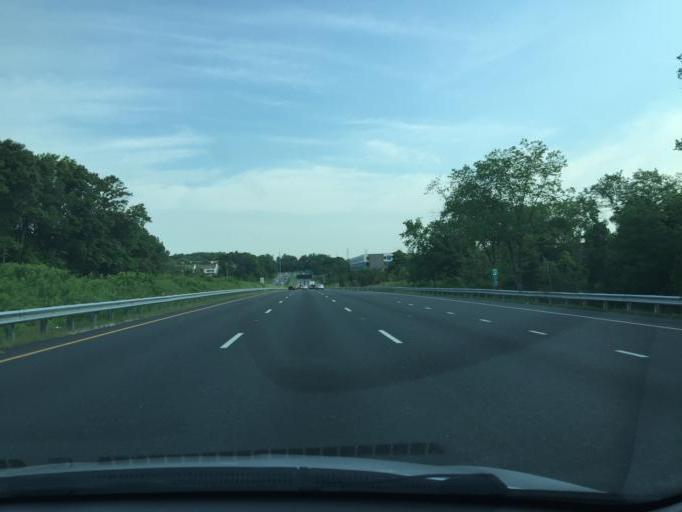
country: US
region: Maryland
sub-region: Baltimore County
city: Lutherville
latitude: 39.3807
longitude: -76.6607
